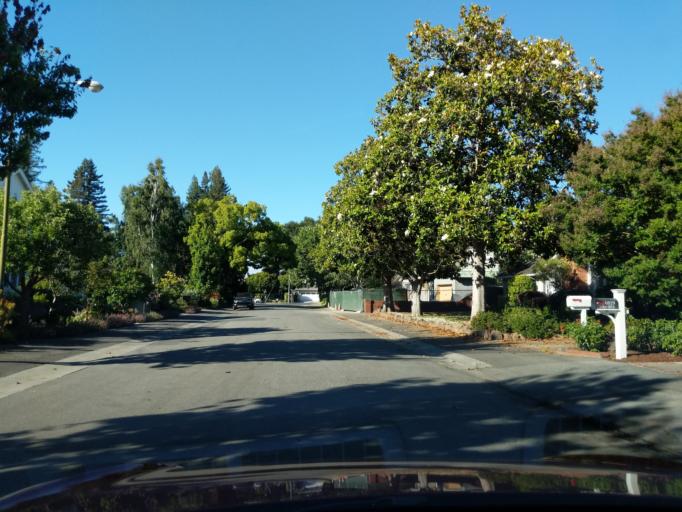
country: US
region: California
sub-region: San Mateo County
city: West Menlo Park
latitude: 37.4340
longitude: -122.1937
